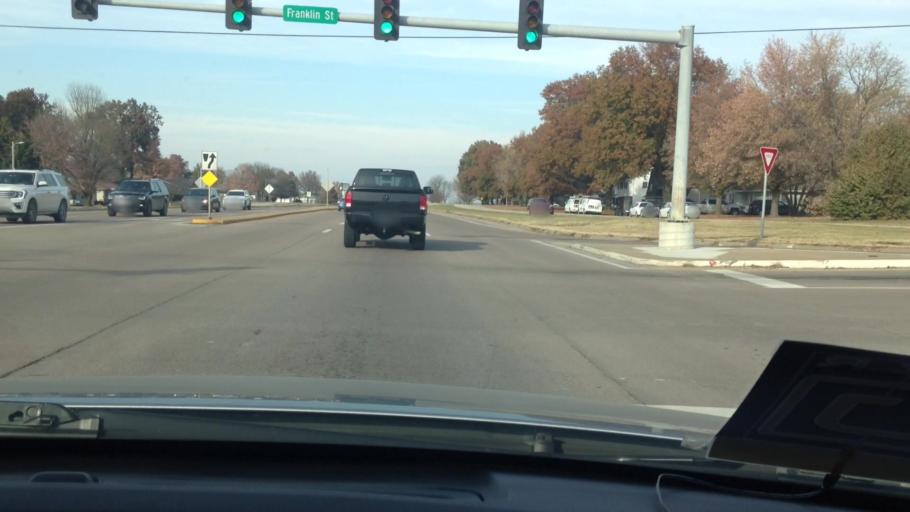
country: US
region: Missouri
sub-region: Henry County
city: Clinton
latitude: 38.3697
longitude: -93.7518
